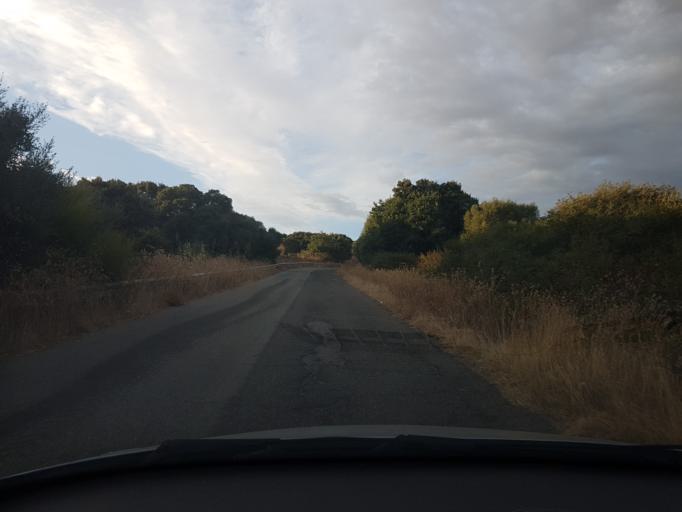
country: IT
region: Sardinia
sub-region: Provincia di Oristano
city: Seneghe
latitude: 40.1004
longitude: 8.6210
